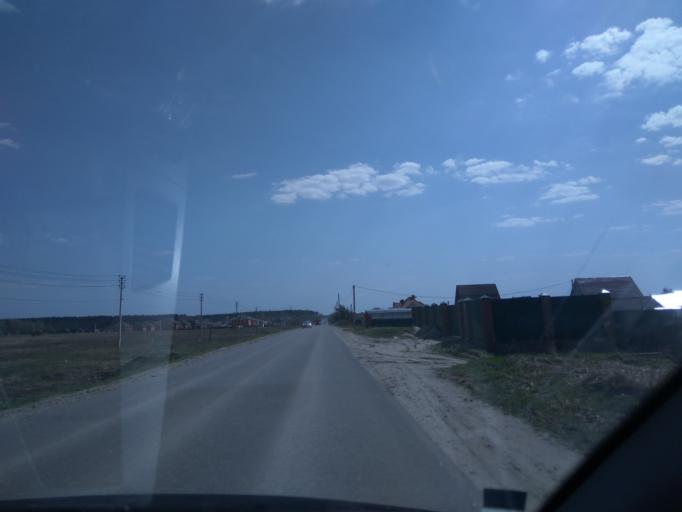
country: RU
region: Moskovskaya
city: Ramenskoye
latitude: 55.5744
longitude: 38.2888
